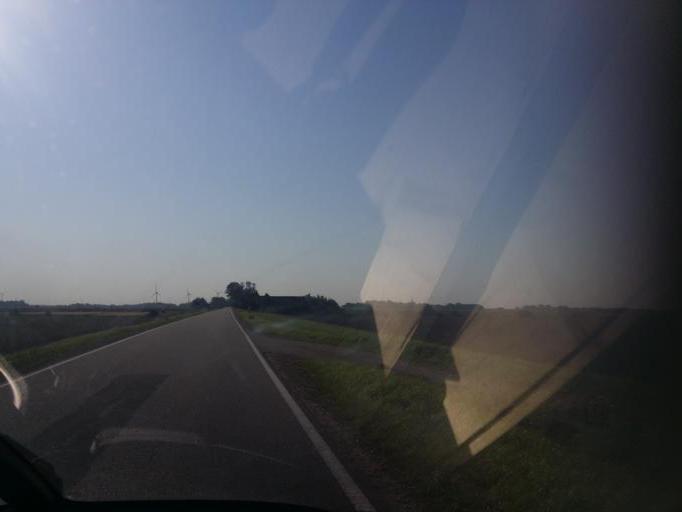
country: DE
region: Schleswig-Holstein
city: Emmelsbull-Horsbull
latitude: 54.7938
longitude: 8.7236
